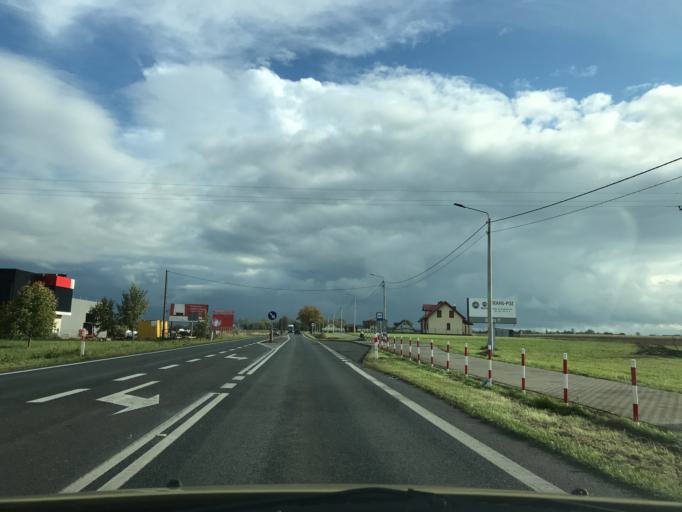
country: PL
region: Greater Poland Voivodeship
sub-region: Powiat ostrowski
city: Nowe Skalmierzyce
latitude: 51.7822
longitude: 18.0126
